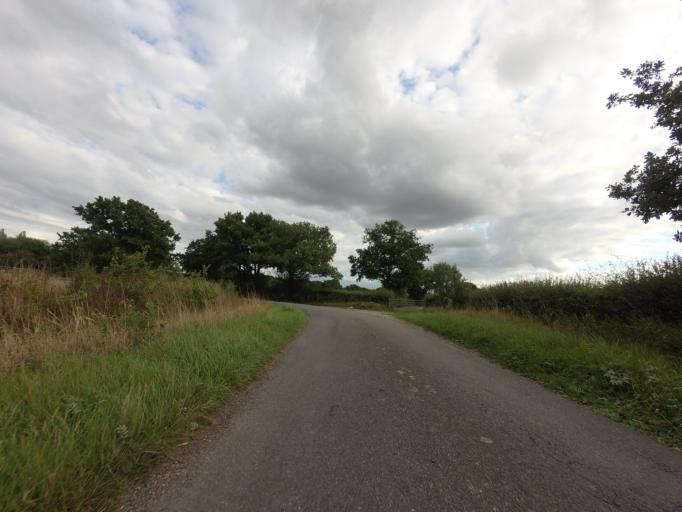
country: GB
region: England
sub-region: Kent
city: Staplehurst
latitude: 51.1868
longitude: 0.5746
